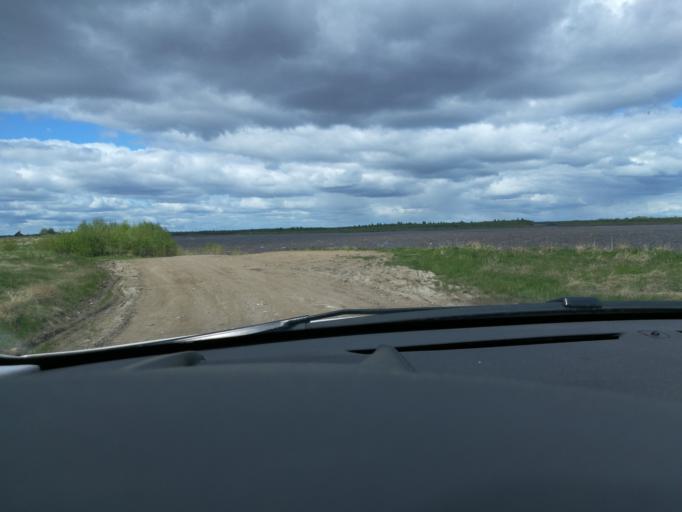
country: RU
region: Arkhangelskaya
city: Lukovetskiy
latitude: 64.2589
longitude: 41.8028
